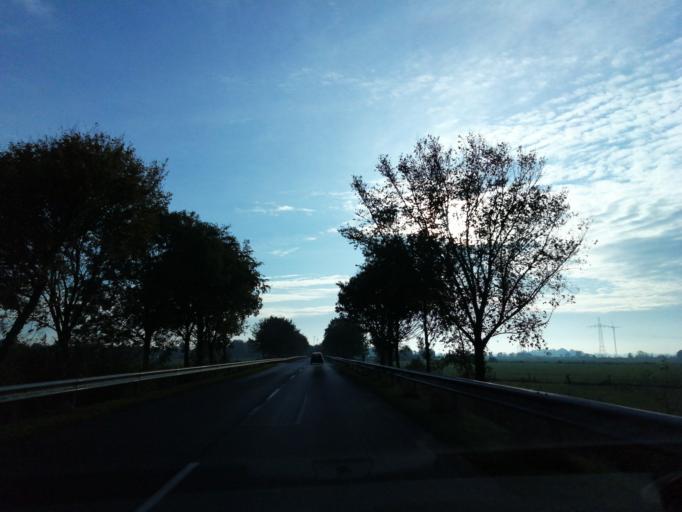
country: DE
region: Lower Saxony
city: Sillenstede
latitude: 53.6234
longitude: 8.0180
